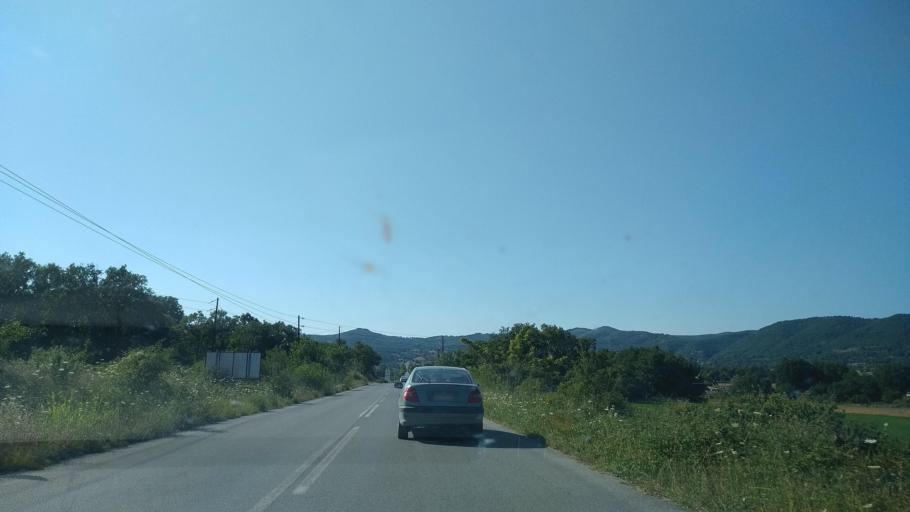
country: GR
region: Central Macedonia
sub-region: Nomos Chalkidikis
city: Megali Panagia
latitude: 40.4155
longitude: 23.6933
